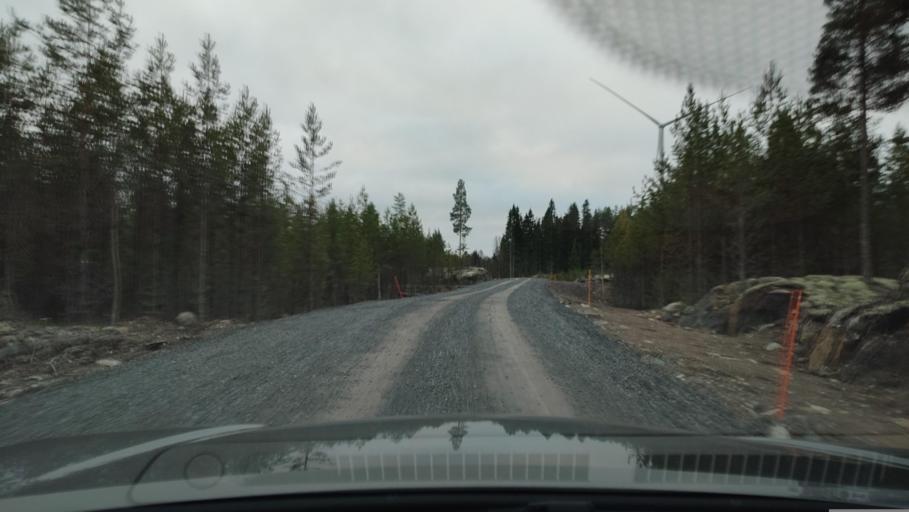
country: FI
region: Southern Ostrobothnia
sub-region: Suupohja
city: Karijoki
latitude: 62.1857
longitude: 21.5739
